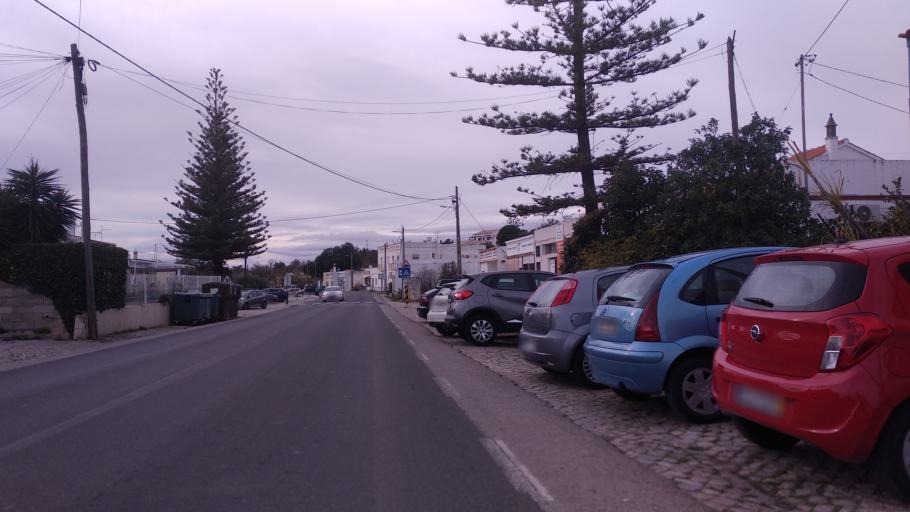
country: PT
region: Faro
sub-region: Loule
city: Loule
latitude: 37.1388
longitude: -7.9930
